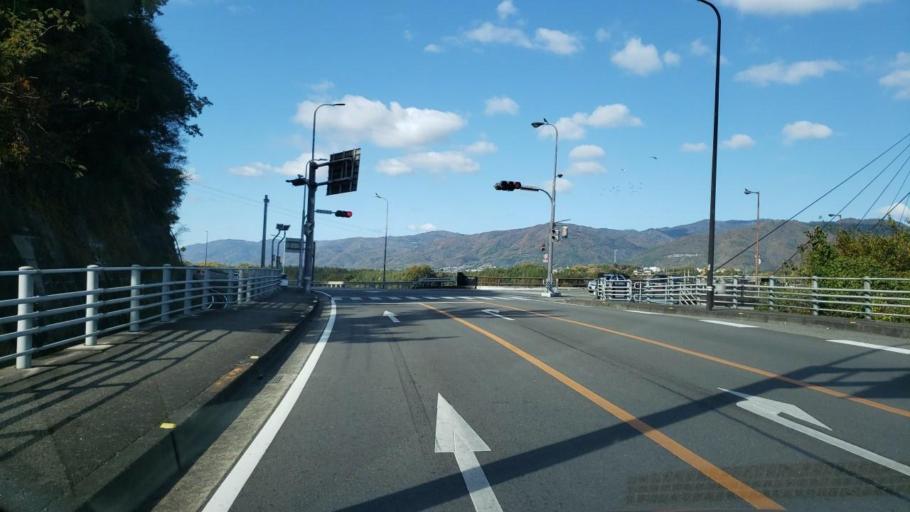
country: JP
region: Tokushima
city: Wakimachi
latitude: 34.0640
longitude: 134.1955
